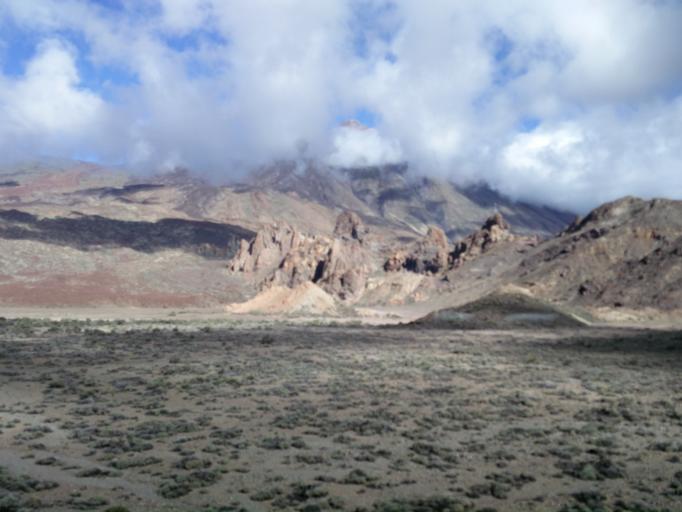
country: ES
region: Canary Islands
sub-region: Provincia de Santa Cruz de Tenerife
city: Vilaflor
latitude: 28.2117
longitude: -16.6327
